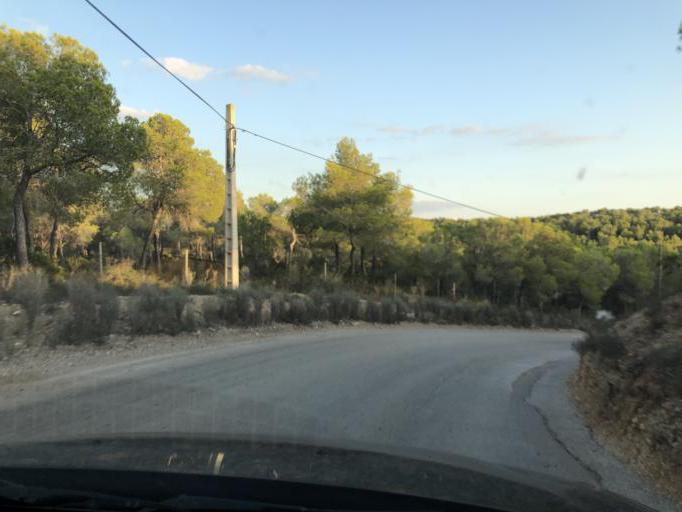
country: ES
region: Balearic Islands
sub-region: Illes Balears
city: Santa Ponsa
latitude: 39.5329
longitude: 2.4808
